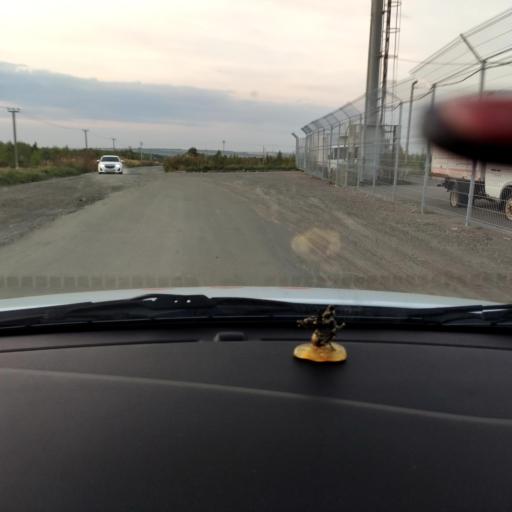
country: RU
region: Tatarstan
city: Vysokaya Gora
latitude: 55.8060
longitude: 49.3142
